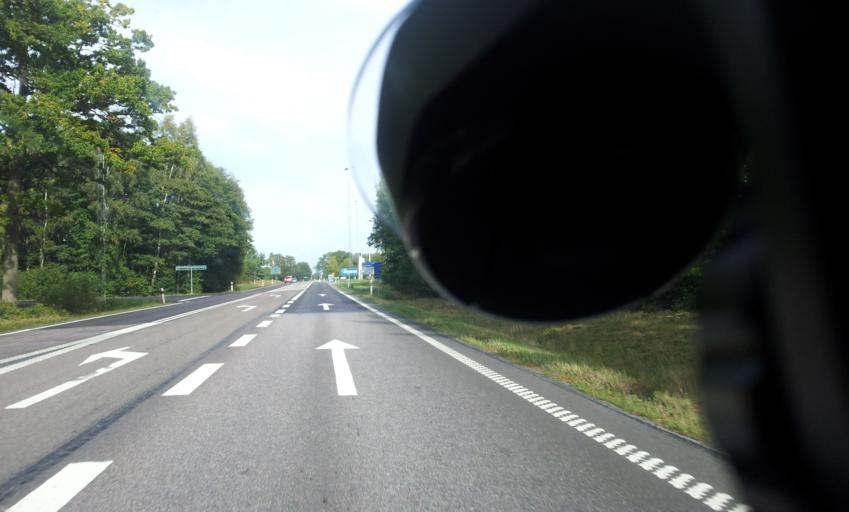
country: SE
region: Kalmar
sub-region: Monsteras Kommun
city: Moensteras
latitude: 57.0217
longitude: 16.4294
